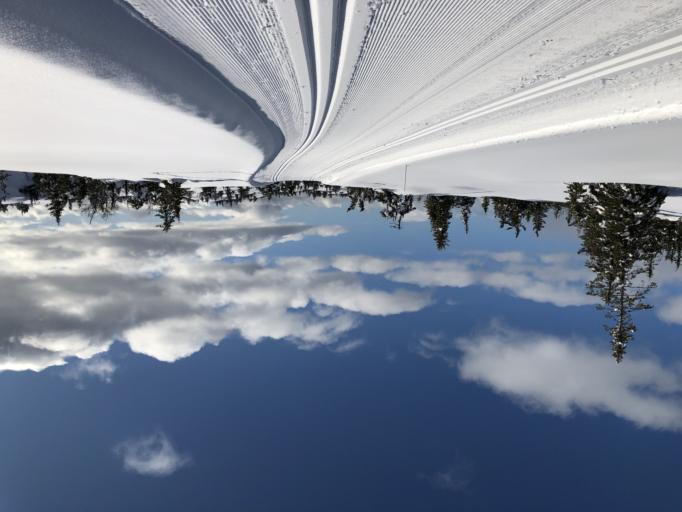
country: NO
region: Oppland
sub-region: Gausdal
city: Segalstad bru
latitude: 61.3316
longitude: 10.0314
